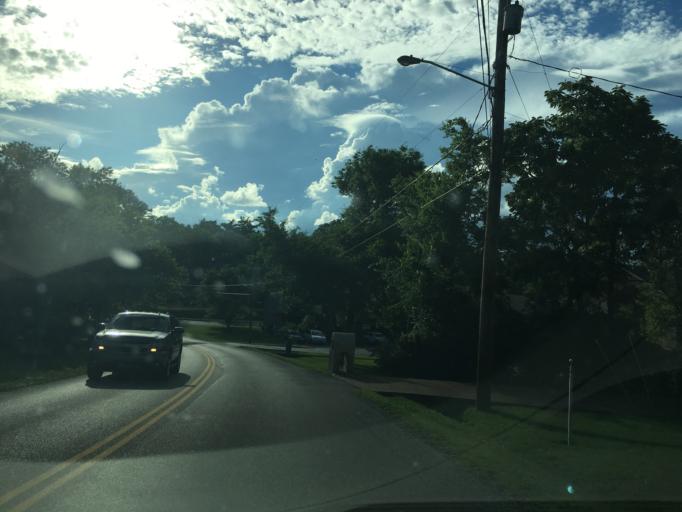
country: US
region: Tennessee
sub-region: Davidson County
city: Oak Hill
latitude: 36.0668
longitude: -86.7233
